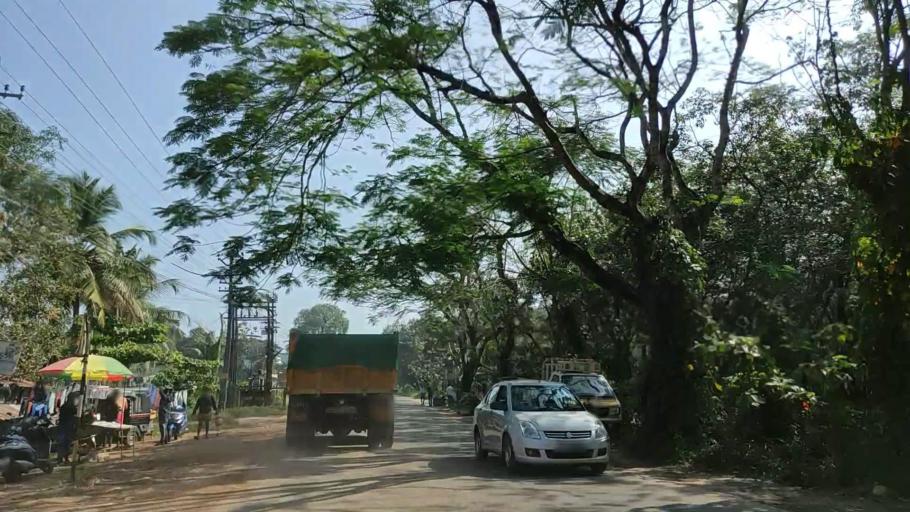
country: IN
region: Kerala
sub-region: Kollam
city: Punalur
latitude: 8.9255
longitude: 76.9027
